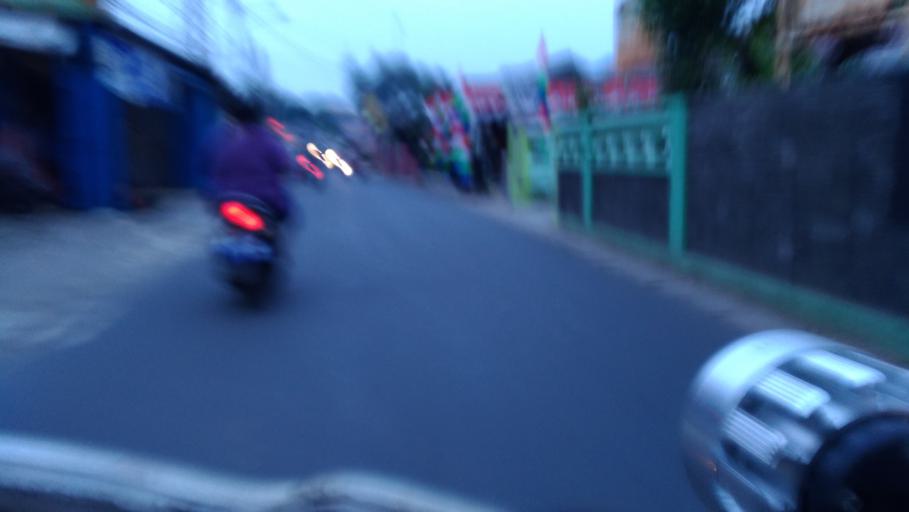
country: ID
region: West Java
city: Depok
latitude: -6.3556
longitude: 106.8791
